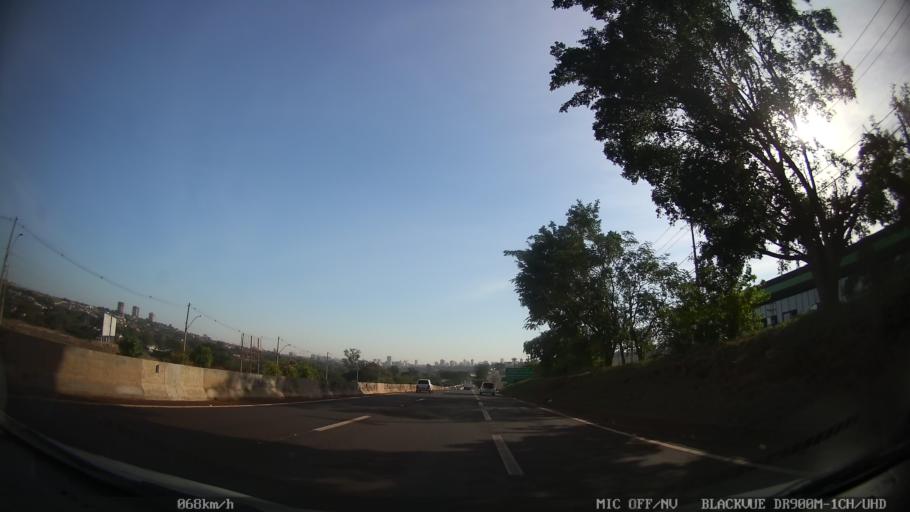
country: BR
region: Sao Paulo
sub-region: Ribeirao Preto
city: Ribeirao Preto
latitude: -21.2518
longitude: -47.8192
